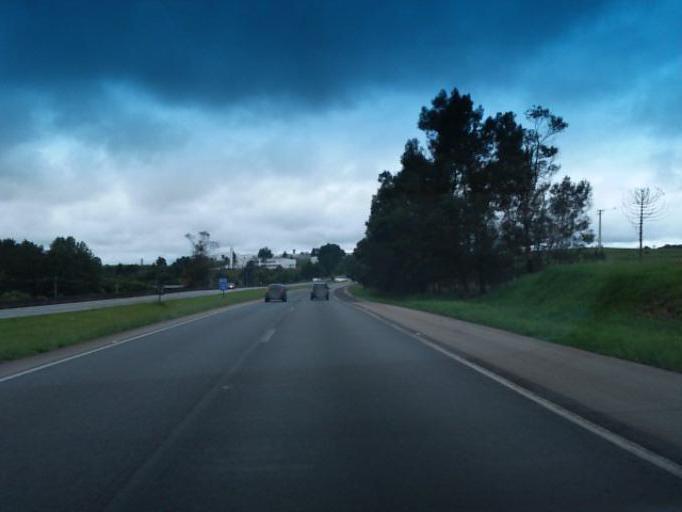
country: BR
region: Parana
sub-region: Quatro Barras
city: Quatro Barras
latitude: -25.3845
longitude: -49.0531
